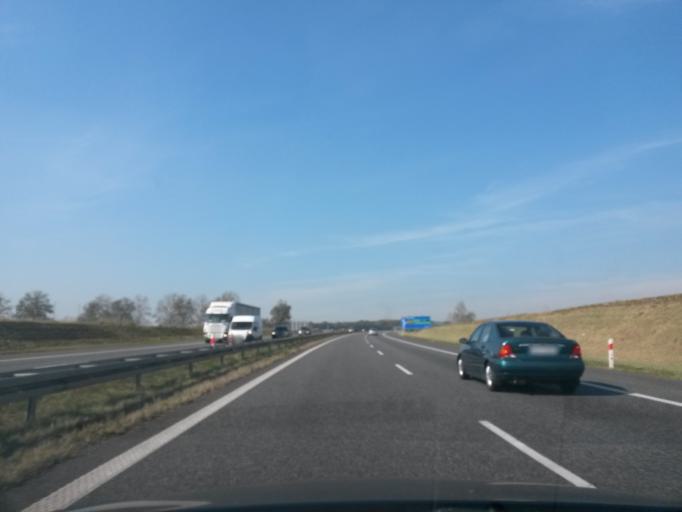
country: PL
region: Silesian Voivodeship
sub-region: Powiat gliwicki
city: Zernica
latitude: 50.2709
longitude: 18.5801
